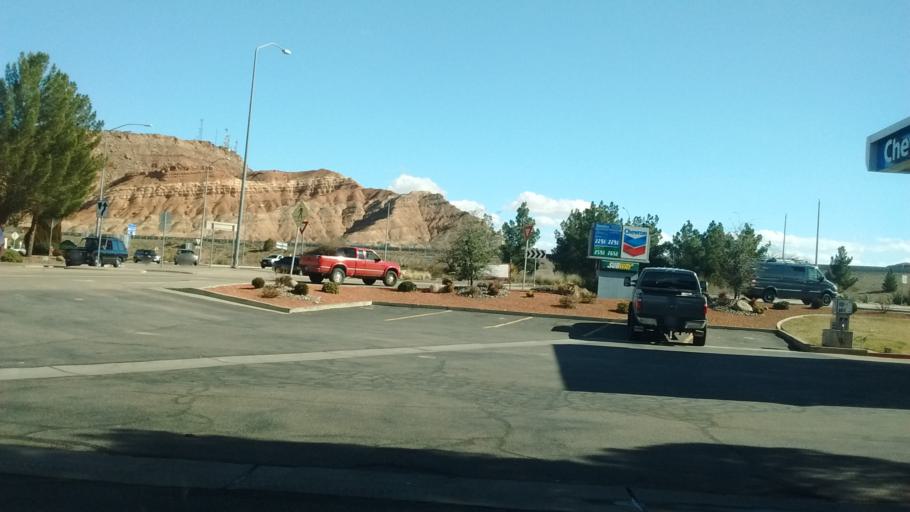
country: US
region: Utah
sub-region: Washington County
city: Saint George
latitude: 37.0601
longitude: -113.5864
